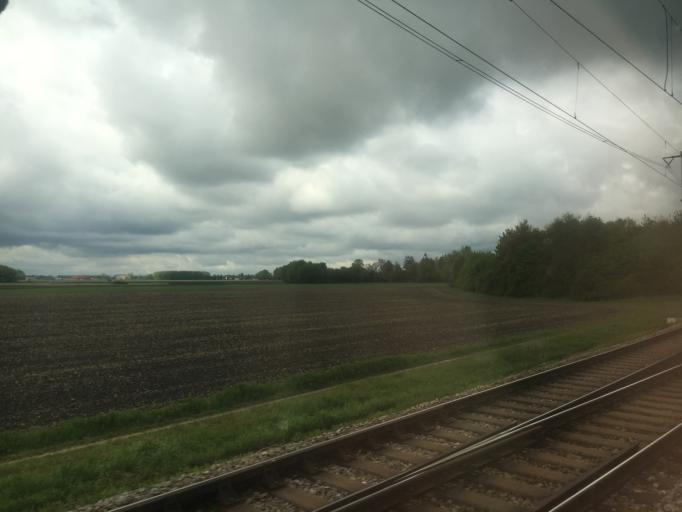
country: DE
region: Bavaria
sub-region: Upper Bavaria
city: Hallbergmoos
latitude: 48.3505
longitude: 11.7420
